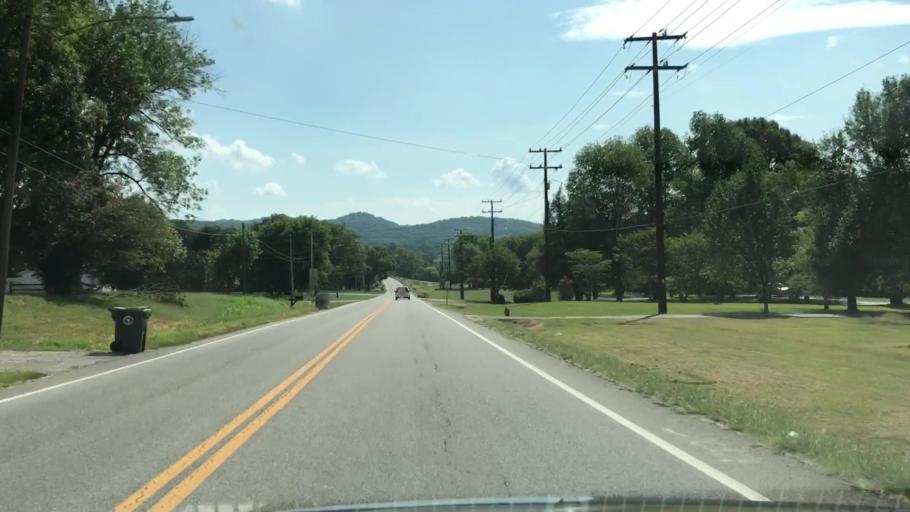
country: US
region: Tennessee
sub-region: Trousdale County
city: Hartsville
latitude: 36.3867
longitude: -86.1354
